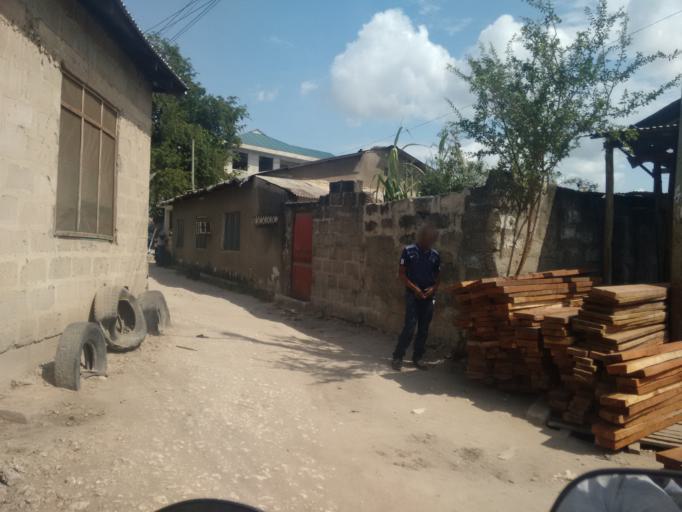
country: TZ
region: Dar es Salaam
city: Dar es Salaam
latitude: -6.8415
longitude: 39.2691
